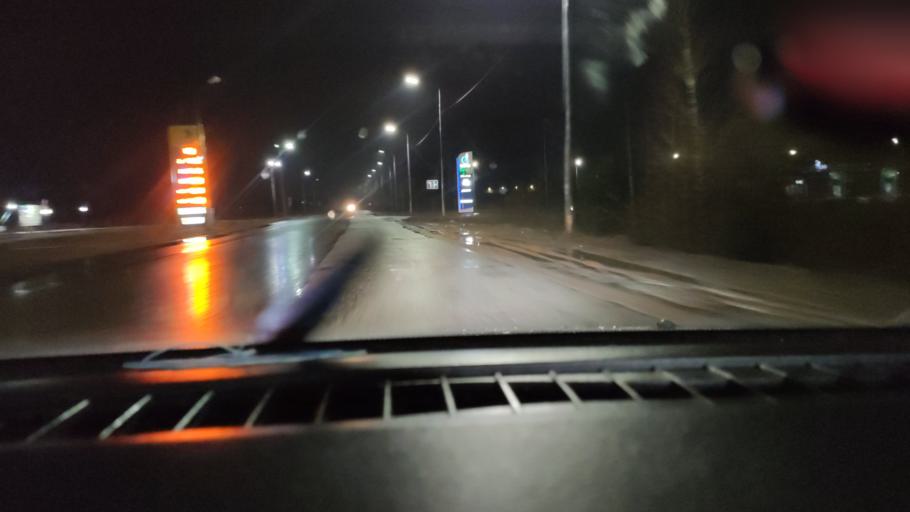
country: RU
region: Udmurtiya
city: Votkinsk
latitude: 57.0367
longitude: 54.0260
